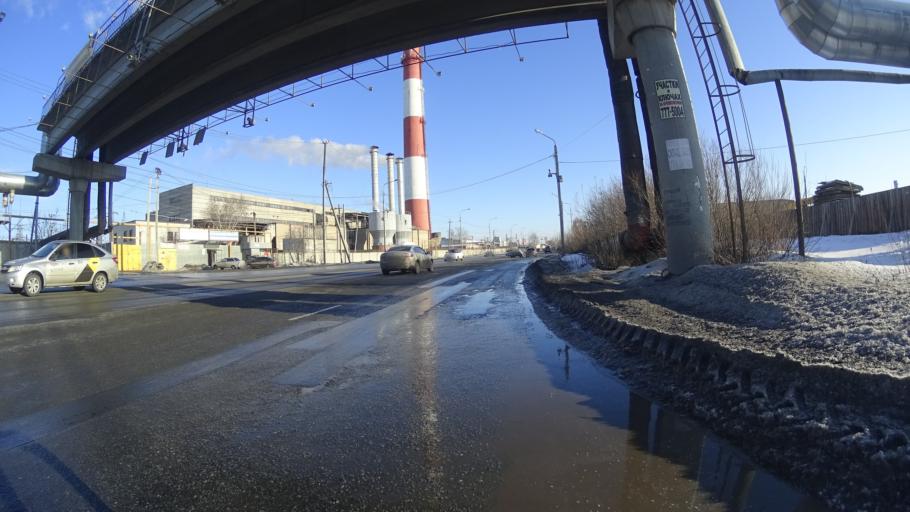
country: RU
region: Chelyabinsk
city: Roshchino
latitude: 55.2078
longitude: 61.3179
